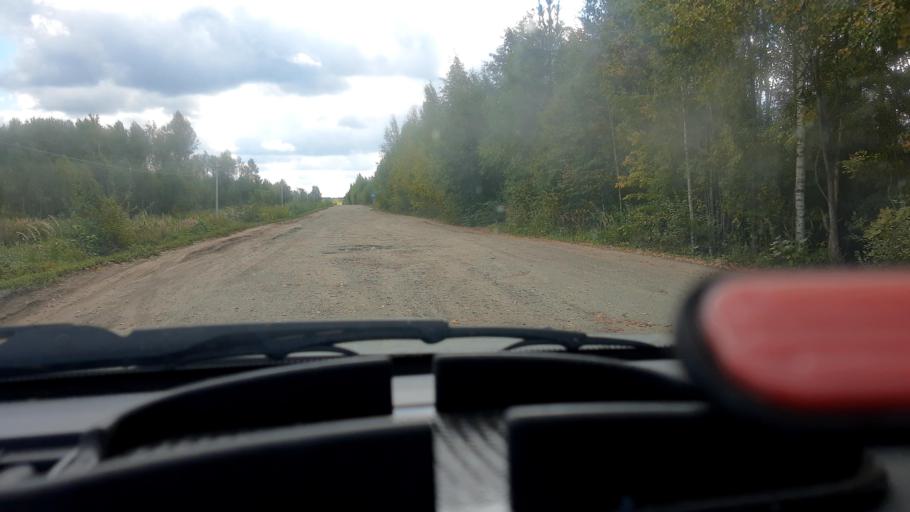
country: RU
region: Mariy-El
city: Kilemary
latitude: 56.8947
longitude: 46.7508
